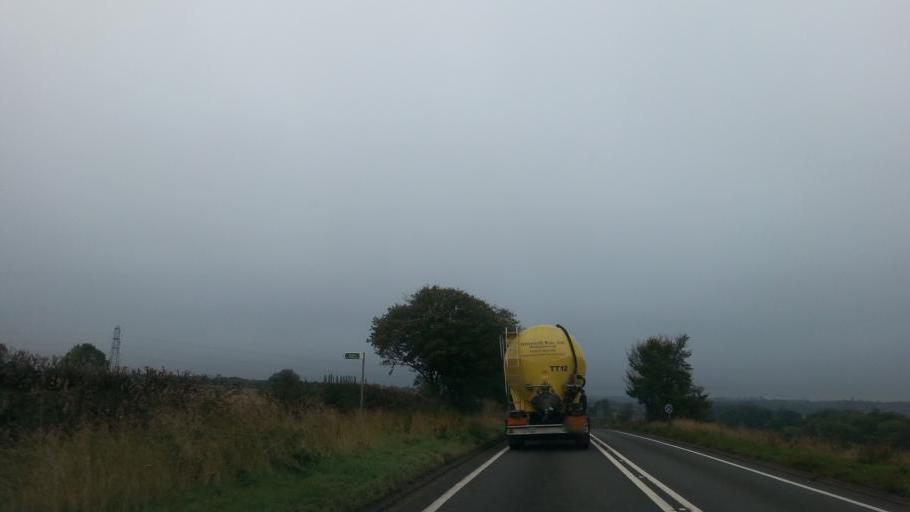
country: GB
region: England
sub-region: Northamptonshire
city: Thrapston
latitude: 52.4092
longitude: -0.5124
